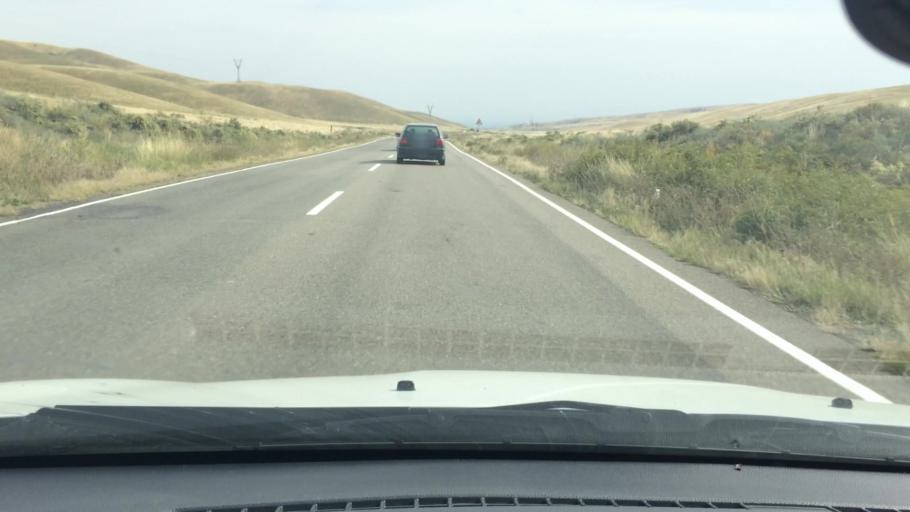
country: GE
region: Kvemo Kartli
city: Rust'avi
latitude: 41.5176
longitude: 44.9428
